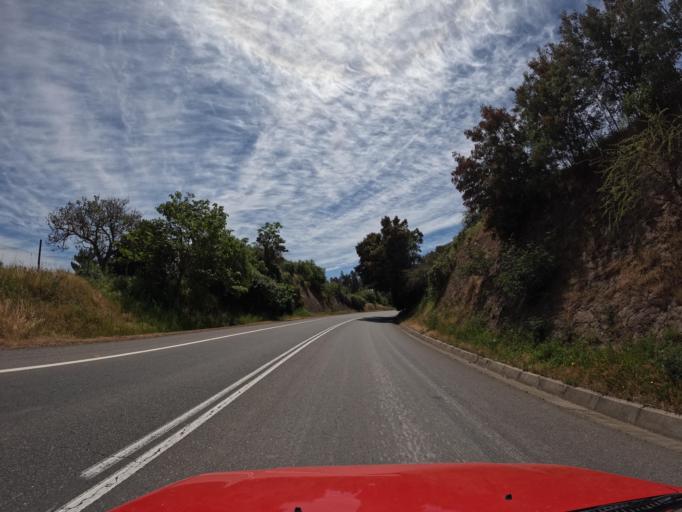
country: CL
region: Maule
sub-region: Provincia de Talca
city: Talca
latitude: -35.2928
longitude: -71.5308
